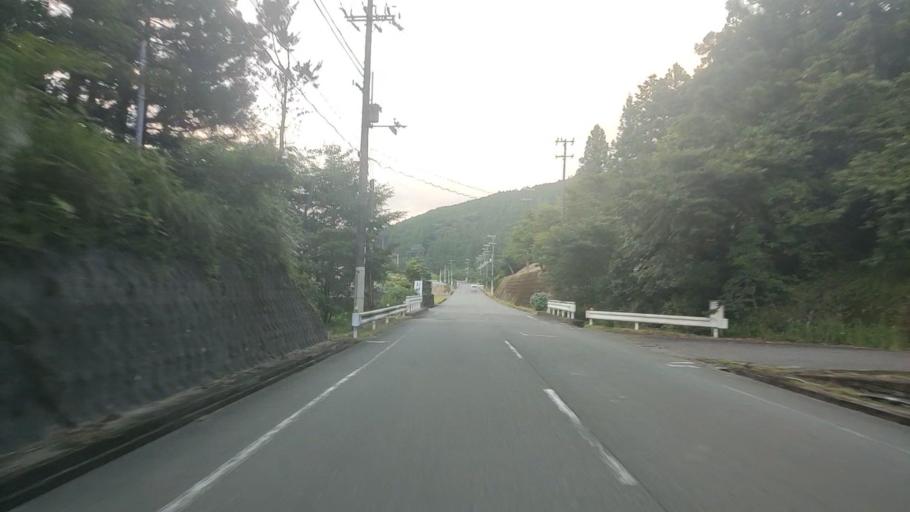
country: JP
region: Wakayama
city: Tanabe
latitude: 33.8205
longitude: 135.6275
